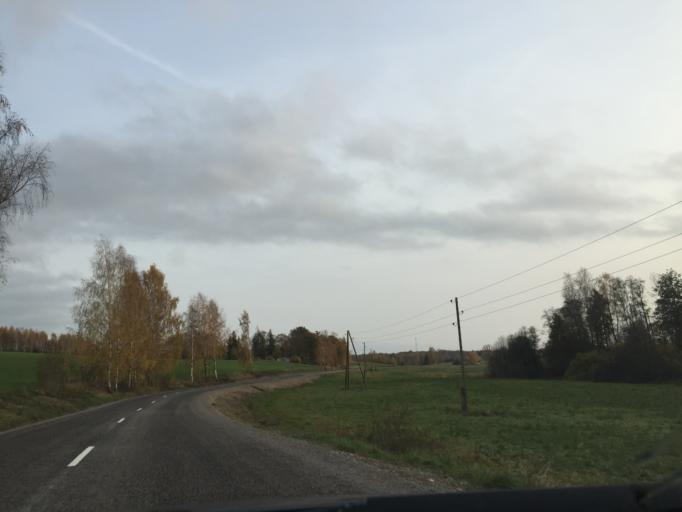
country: LV
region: Pargaujas
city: Stalbe
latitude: 57.3271
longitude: 25.1347
